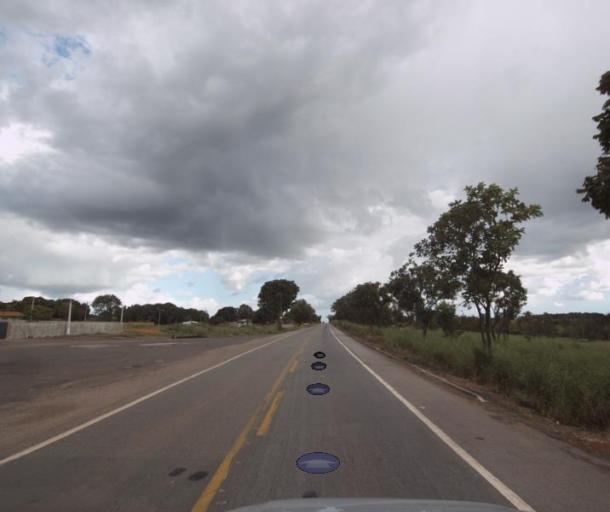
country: BR
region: Goias
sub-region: Porangatu
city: Porangatu
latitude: -13.3136
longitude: -49.1177
